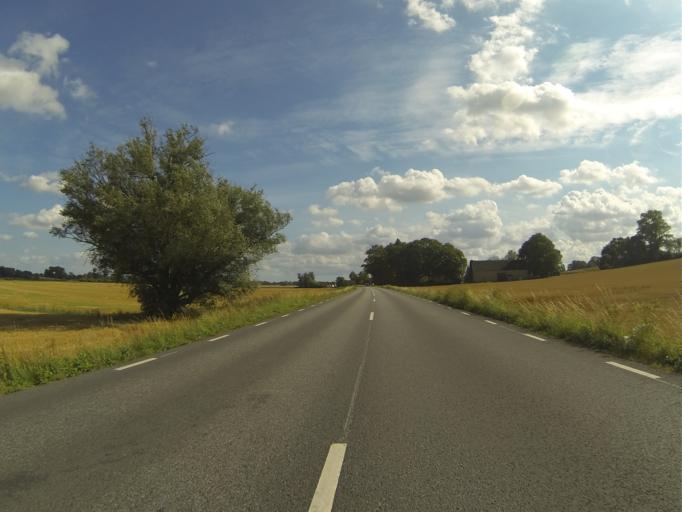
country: SE
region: Skane
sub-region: Eslovs Kommun
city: Eslov
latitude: 55.7561
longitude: 13.3194
